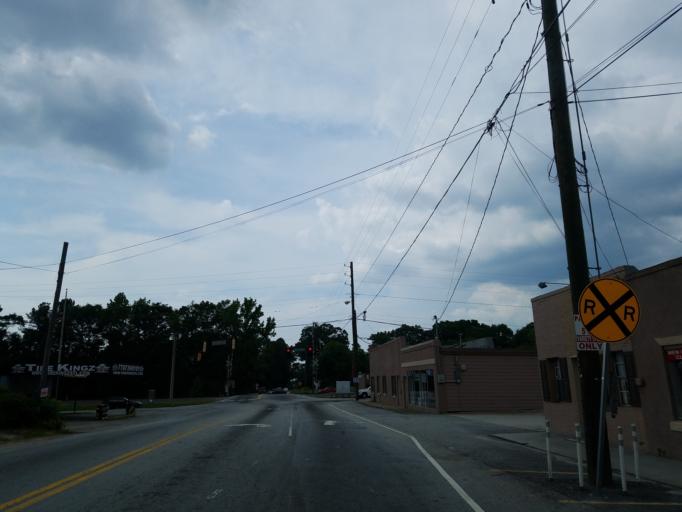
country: US
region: Georgia
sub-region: Douglas County
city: Lithia Springs
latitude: 33.7935
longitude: -84.6605
